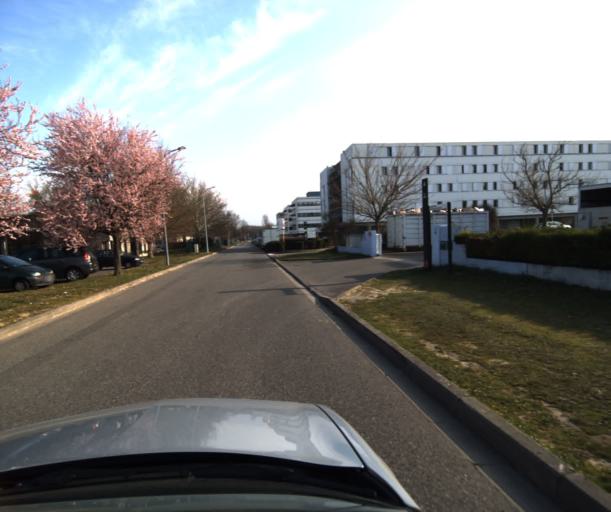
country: FR
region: Midi-Pyrenees
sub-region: Departement de la Haute-Garonne
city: Ramonville-Saint-Agne
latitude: 43.5510
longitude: 1.4844
